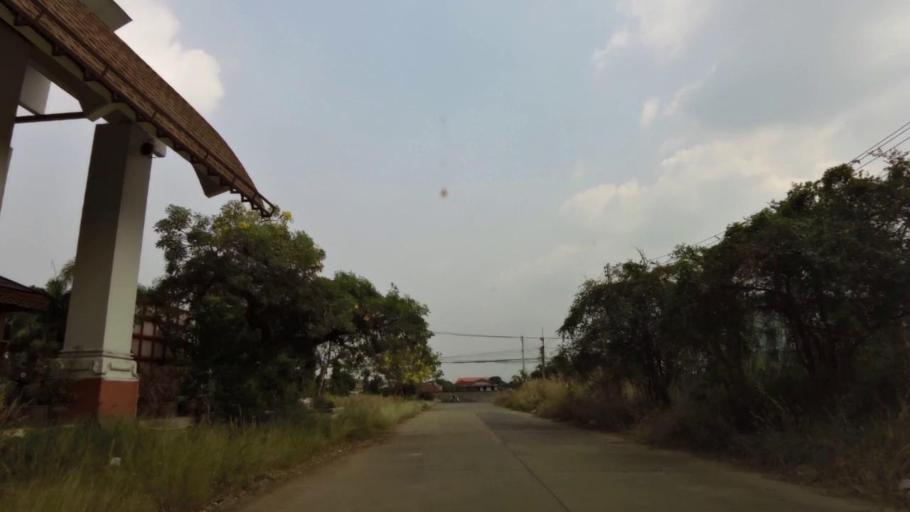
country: TH
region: Phra Nakhon Si Ayutthaya
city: Phra Nakhon Si Ayutthaya
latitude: 14.3378
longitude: 100.5798
